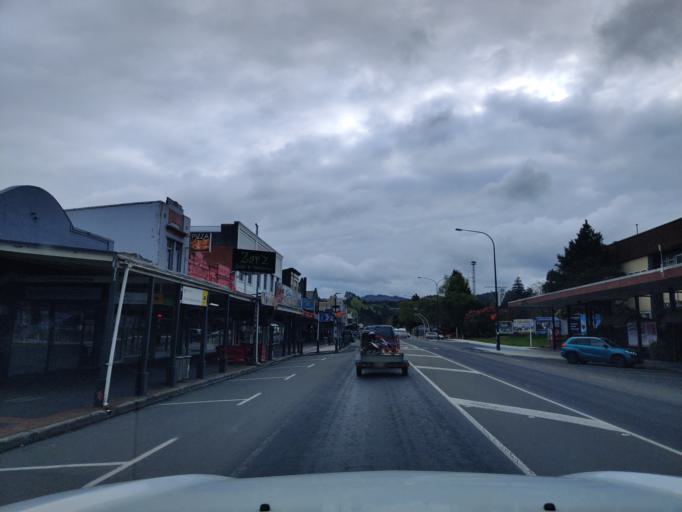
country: NZ
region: Waikato
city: Turangi
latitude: -38.8830
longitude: 175.2651
